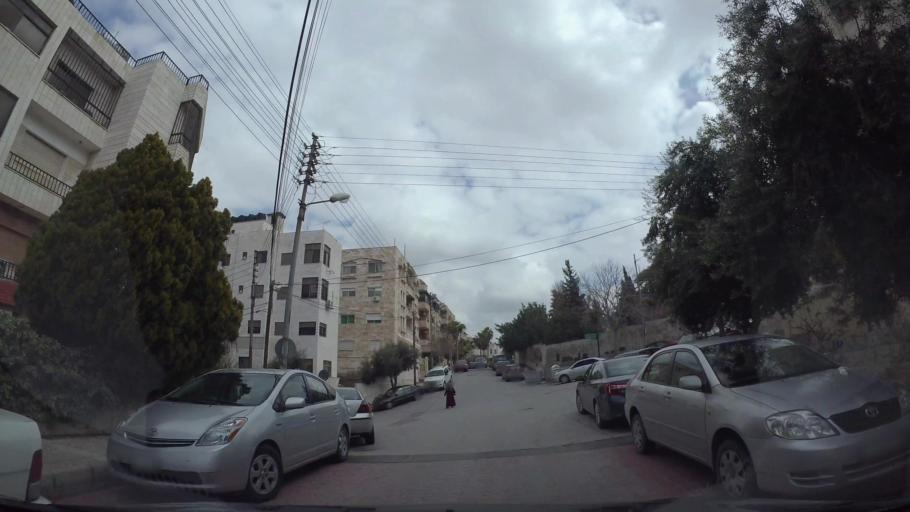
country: JO
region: Amman
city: Amman
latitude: 31.9764
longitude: 35.8999
